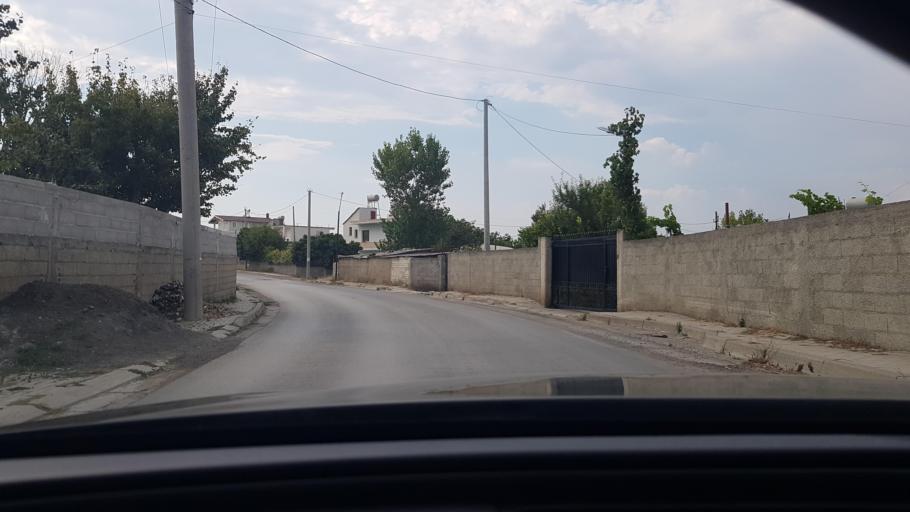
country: AL
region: Durres
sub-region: Rrethi i Durresit
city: Katundi i Ri
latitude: 41.4269
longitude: 19.5475
